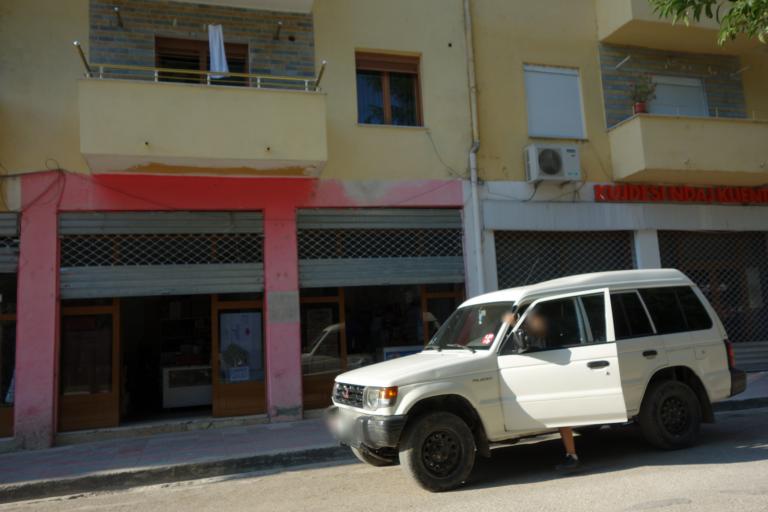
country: AL
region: Berat
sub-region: Rrethi i Skraparit
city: Corovode
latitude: 40.5046
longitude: 20.2240
